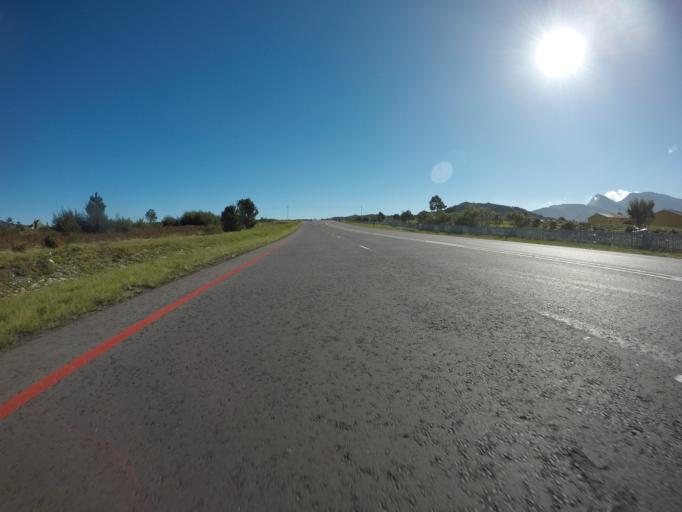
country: ZA
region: Western Cape
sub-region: Overberg District Municipality
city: Grabouw
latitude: -34.1631
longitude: 18.9873
